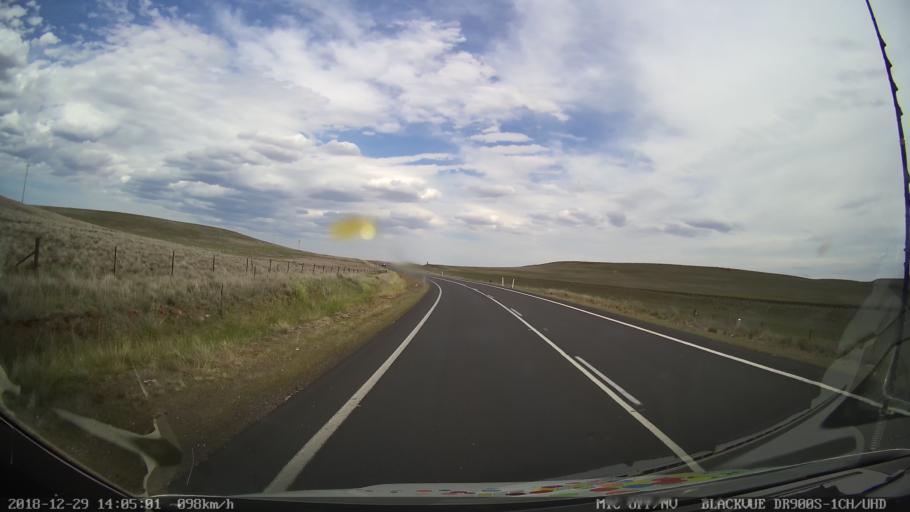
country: AU
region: New South Wales
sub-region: Cooma-Monaro
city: Cooma
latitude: -36.3247
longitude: 149.1889
